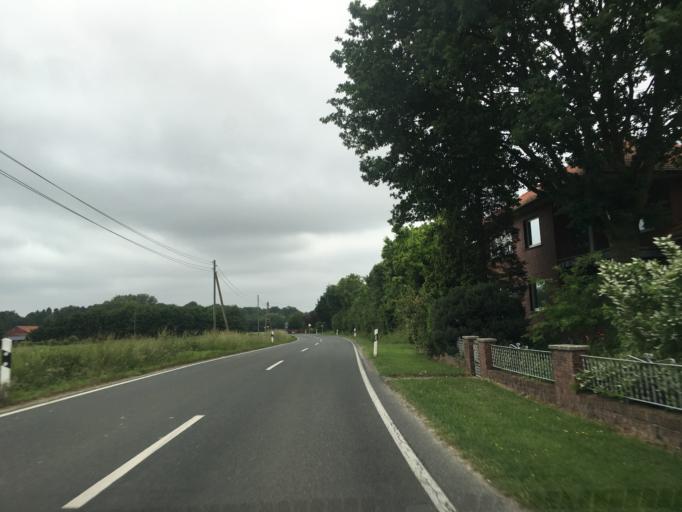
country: DE
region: North Rhine-Westphalia
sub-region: Regierungsbezirk Munster
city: Laer
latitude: 52.0798
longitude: 7.3477
